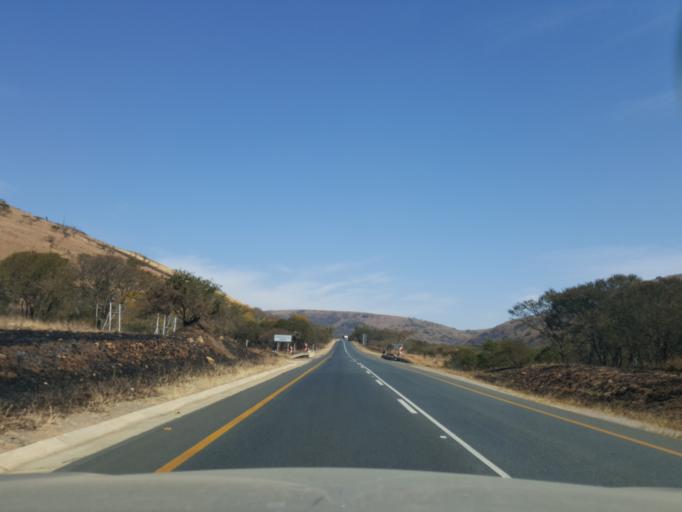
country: ZA
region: Mpumalanga
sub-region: Ehlanzeni District
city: Lydenburg
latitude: -25.4683
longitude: 30.4026
